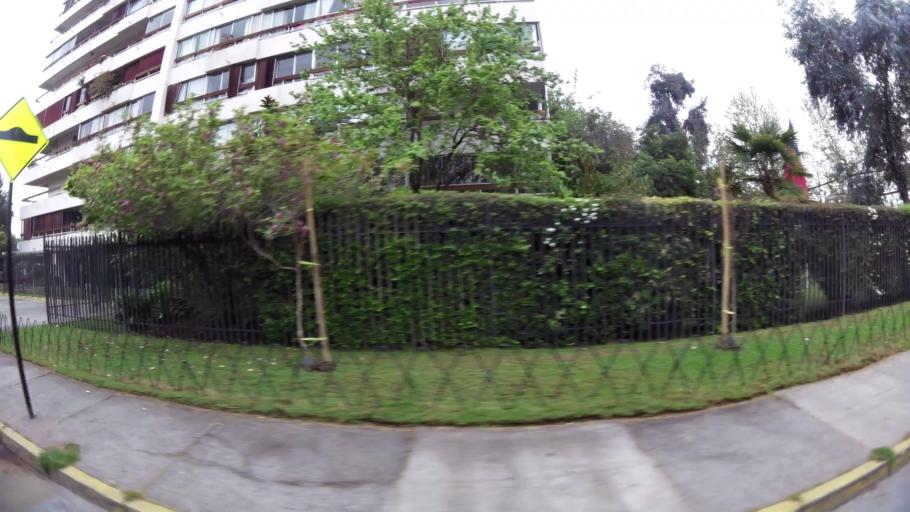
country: CL
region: Santiago Metropolitan
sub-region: Provincia de Santiago
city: Villa Presidente Frei, Nunoa, Santiago, Chile
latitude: -33.3964
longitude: -70.5809
